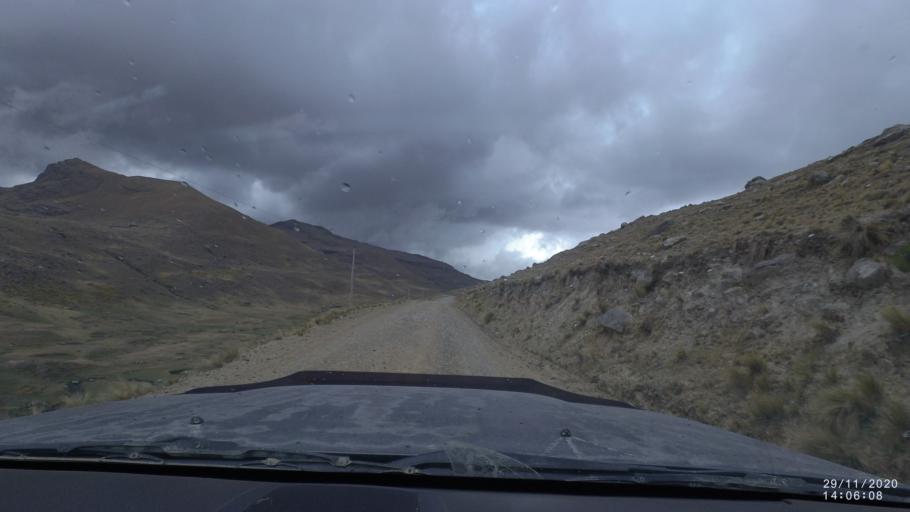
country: BO
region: Cochabamba
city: Sipe Sipe
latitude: -17.2114
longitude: -66.3775
